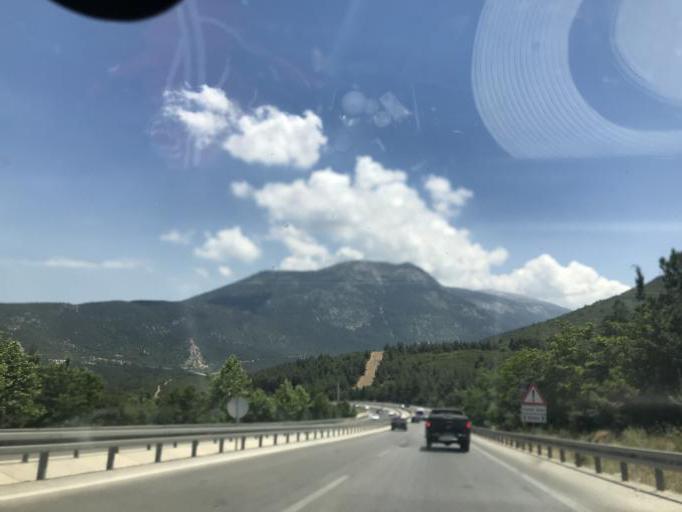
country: TR
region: Denizli
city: Honaz
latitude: 37.7311
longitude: 29.1838
